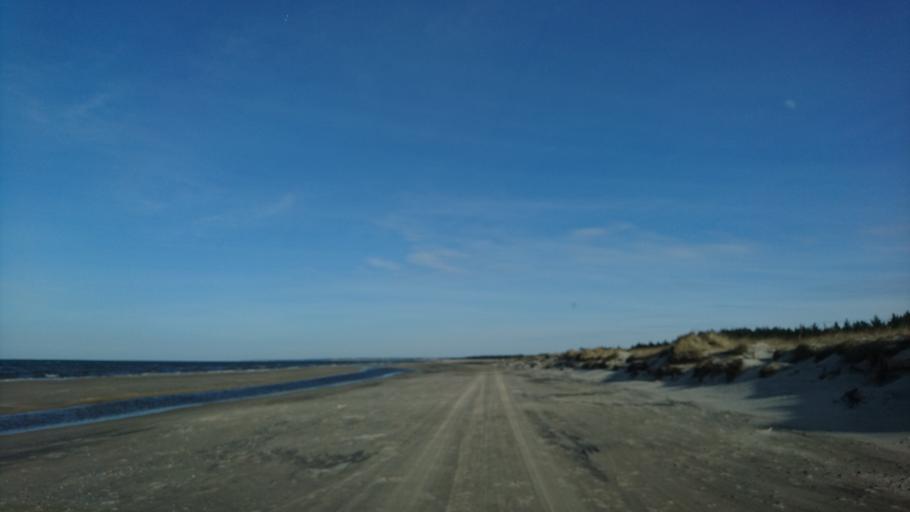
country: DK
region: North Denmark
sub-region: Hjorring Kommune
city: Hirtshals
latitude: 57.5909
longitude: 10.0545
